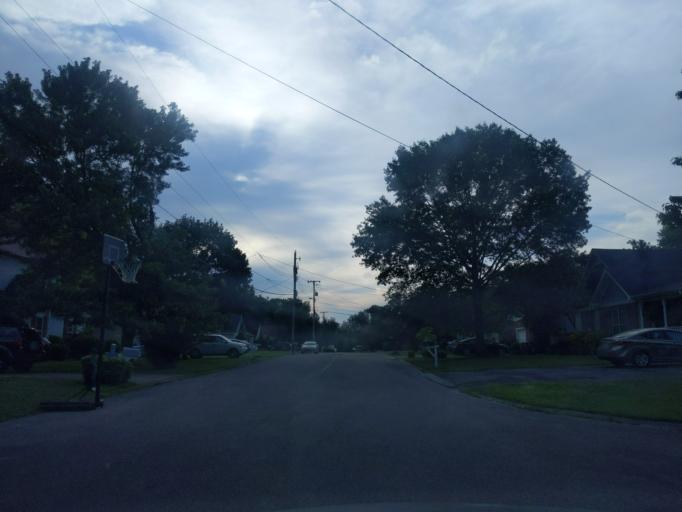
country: US
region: Tennessee
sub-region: Davidson County
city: Lakewood
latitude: 36.1850
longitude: -86.6045
